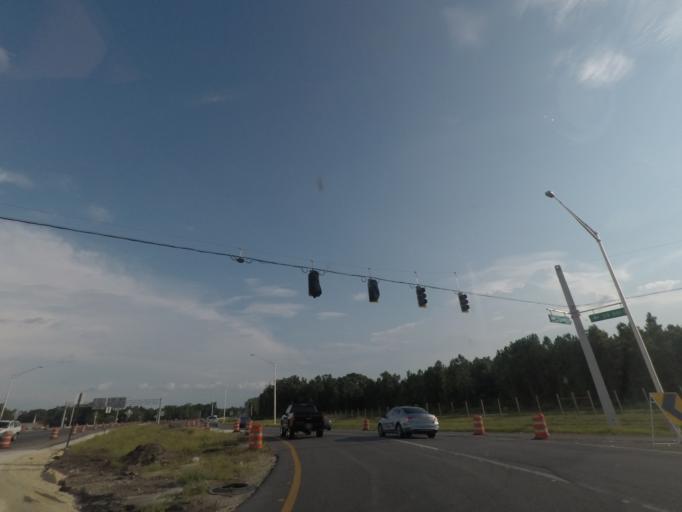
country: US
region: Florida
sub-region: Bradford County
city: Starke
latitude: 29.9160
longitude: -82.1344
